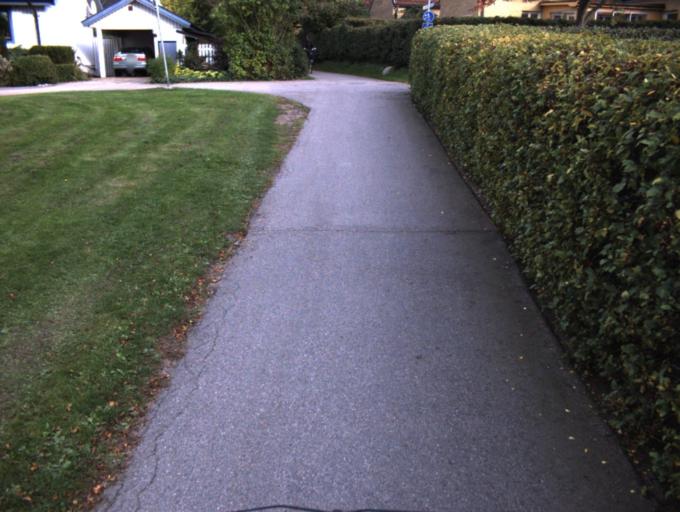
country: SE
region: Skane
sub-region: Helsingborg
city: Rydeback
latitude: 56.0182
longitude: 12.7444
